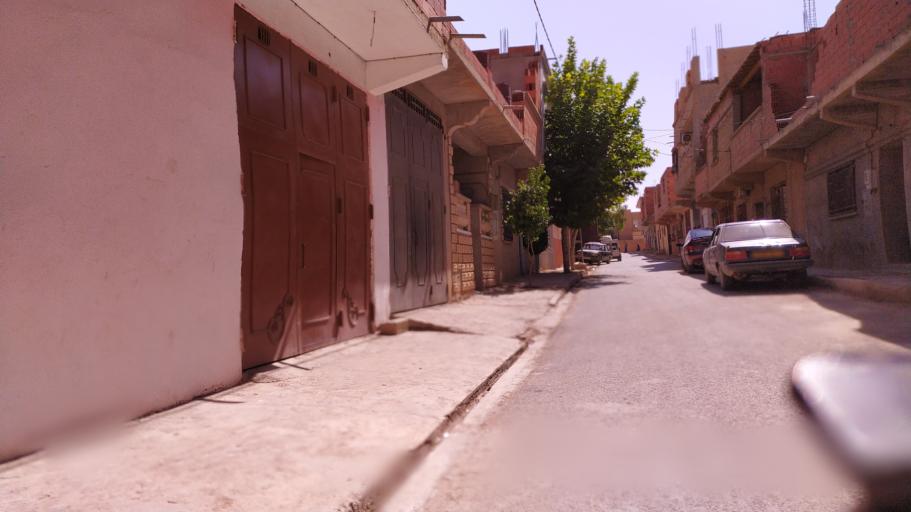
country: DZ
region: Tiaret
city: Frenda
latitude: 34.8967
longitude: 1.2387
